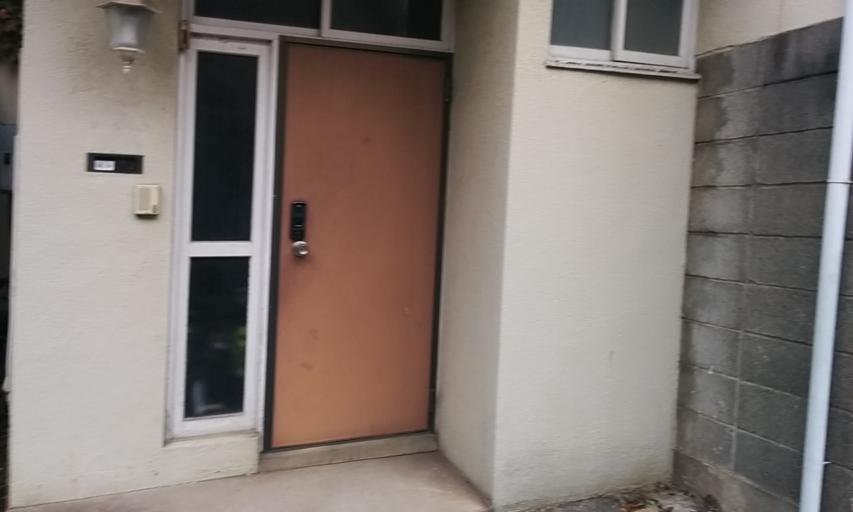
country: JP
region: Tokyo
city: Tokyo
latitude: 35.7042
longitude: 139.7241
